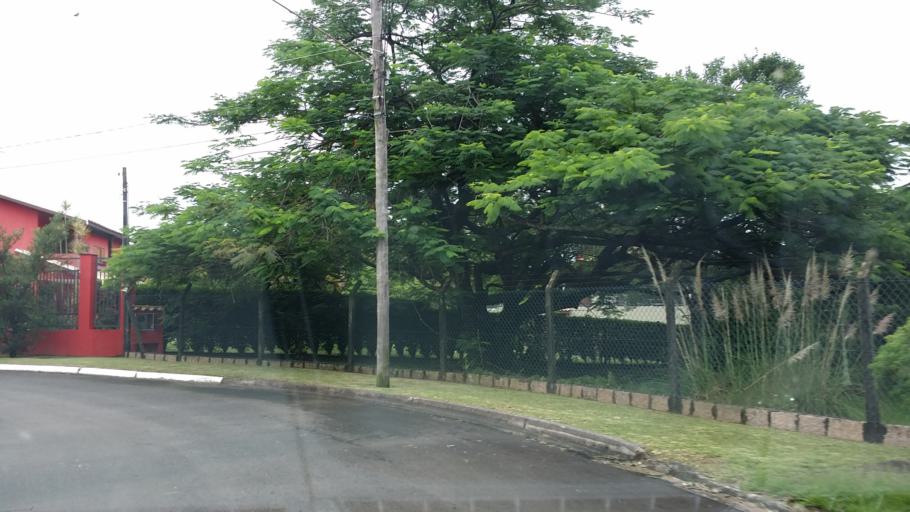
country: BR
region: Sao Paulo
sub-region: Indaiatuba
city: Indaiatuba
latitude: -23.1436
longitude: -47.1817
